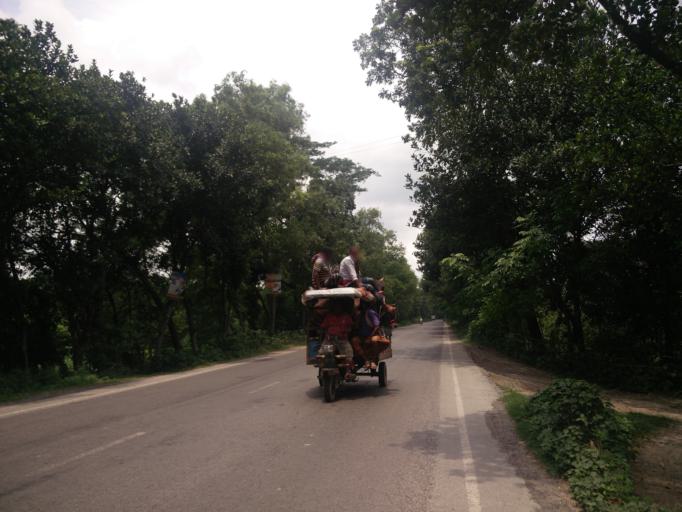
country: BD
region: Khulna
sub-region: Magura
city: Magura
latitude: 23.5458
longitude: 89.5253
